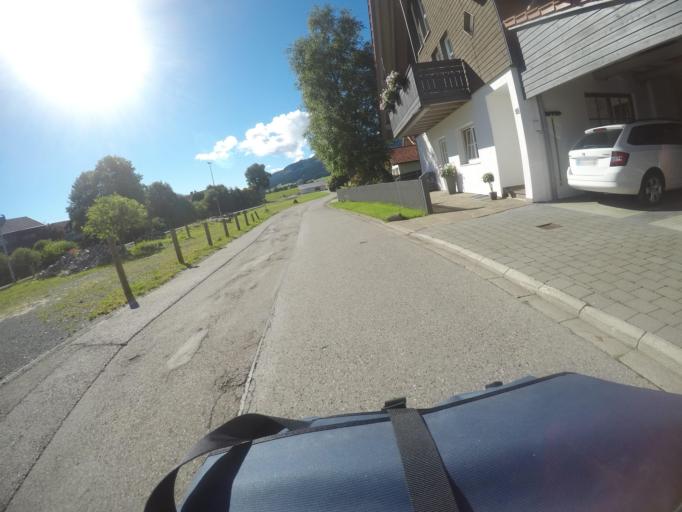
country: DE
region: Bavaria
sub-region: Swabia
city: Oy-Mittelberg
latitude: 47.6284
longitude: 10.4604
